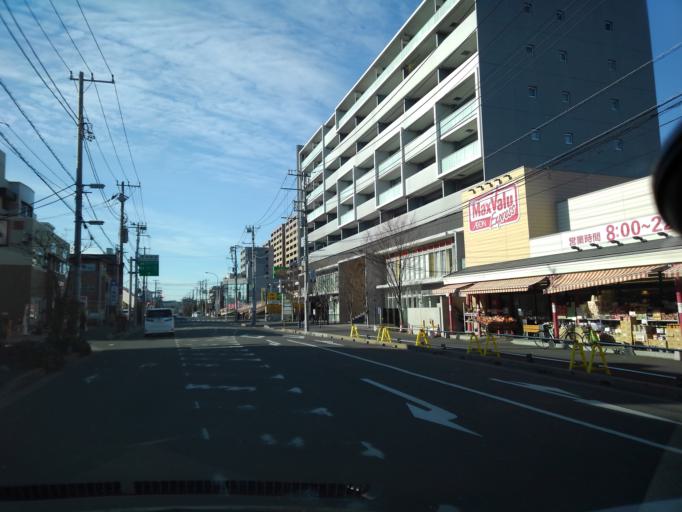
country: JP
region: Chiba
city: Funabashi
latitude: 35.6569
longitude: 140.0547
